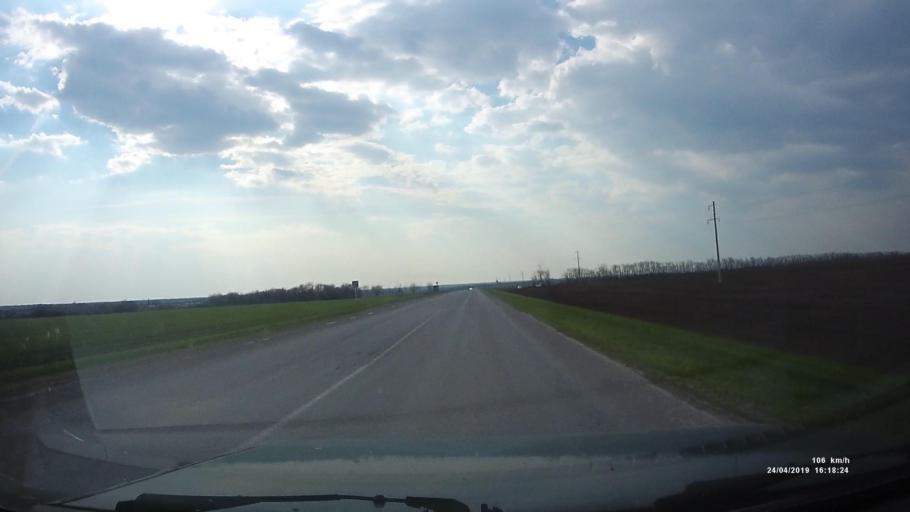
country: RU
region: Rostov
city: Sovetskoye
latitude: 46.7743
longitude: 42.1169
